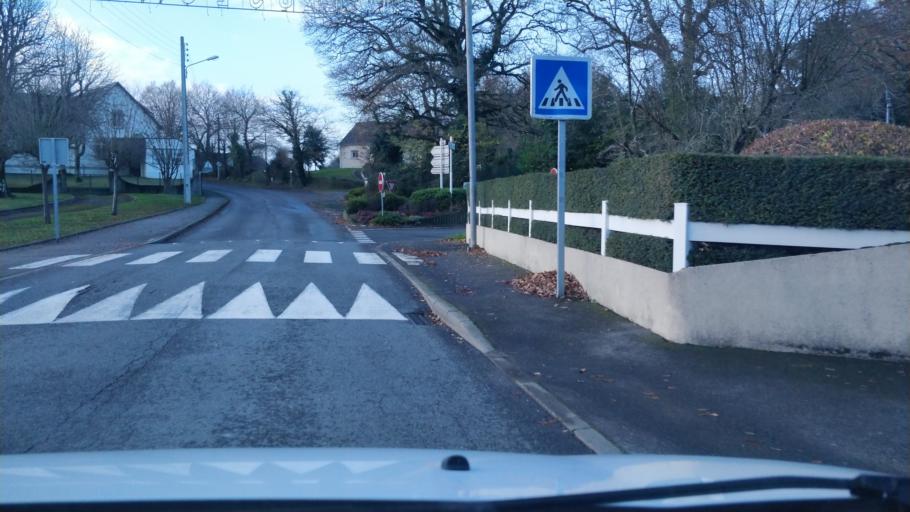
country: FR
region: Pays de la Loire
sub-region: Departement de la Loire-Atlantique
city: Asserac
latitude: 47.4278
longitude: -2.3924
